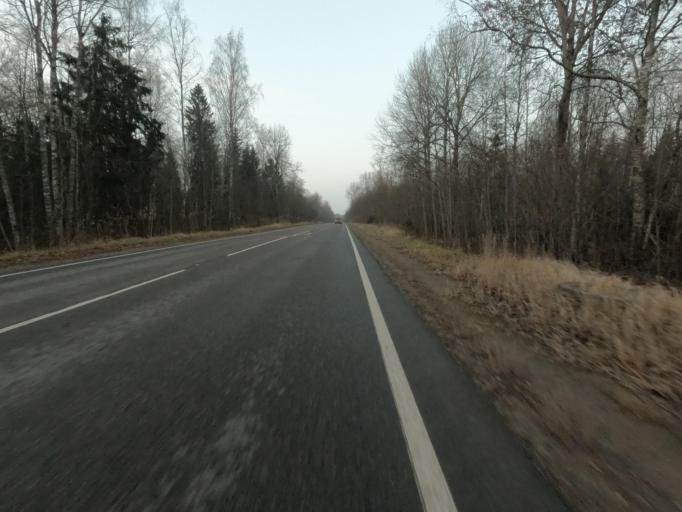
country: RU
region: Leningrad
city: Kirovsk
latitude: 59.8532
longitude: 30.9924
